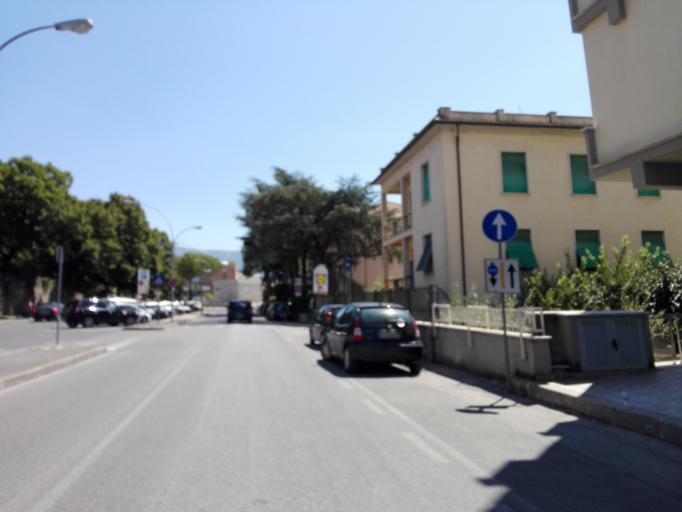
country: IT
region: Umbria
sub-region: Provincia di Perugia
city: Foligno
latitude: 42.9515
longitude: 12.7001
